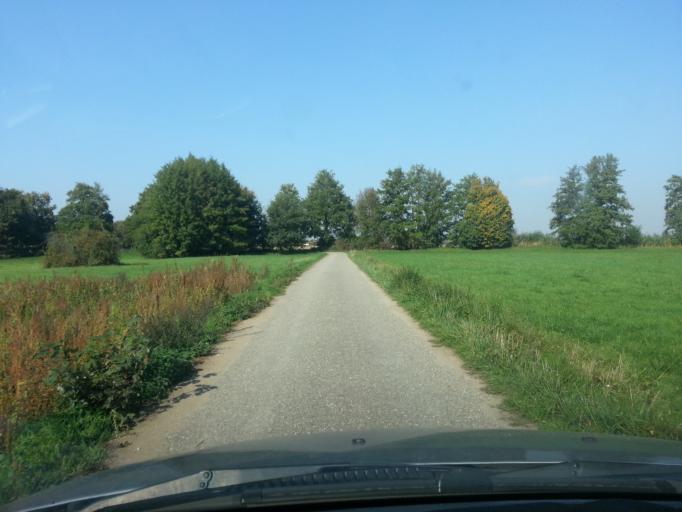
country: DE
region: Rheinland-Pfalz
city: Bohl-Iggelheim
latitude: 49.3749
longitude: 8.3373
